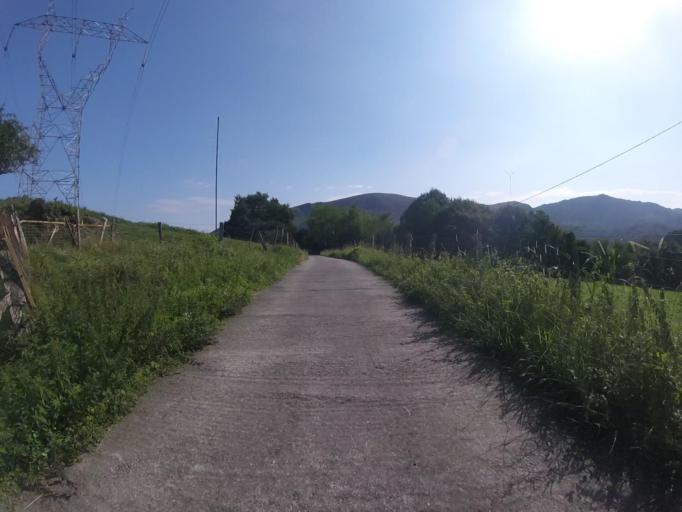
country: ES
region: Basque Country
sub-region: Provincia de Guipuzcoa
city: Irun
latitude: 43.3220
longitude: -1.7471
